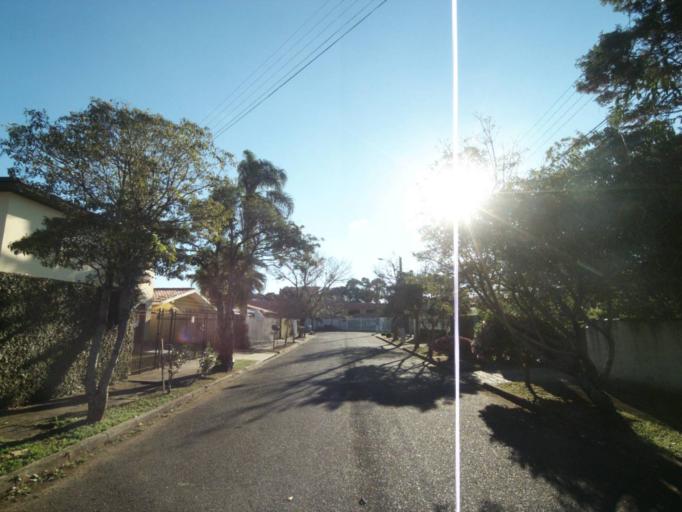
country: BR
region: Parana
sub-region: Curitiba
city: Curitiba
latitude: -25.4589
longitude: -49.3012
